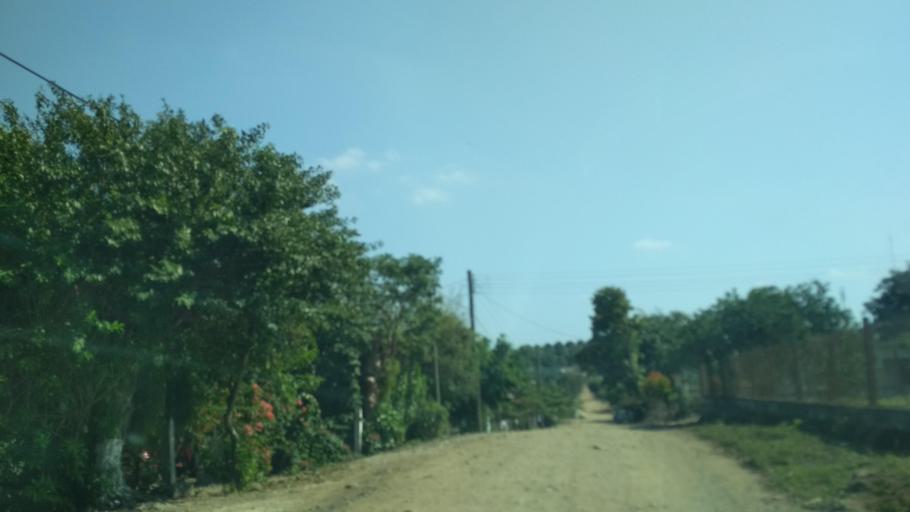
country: MX
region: Puebla
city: San Jose Acateno
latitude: 20.1761
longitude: -97.2313
